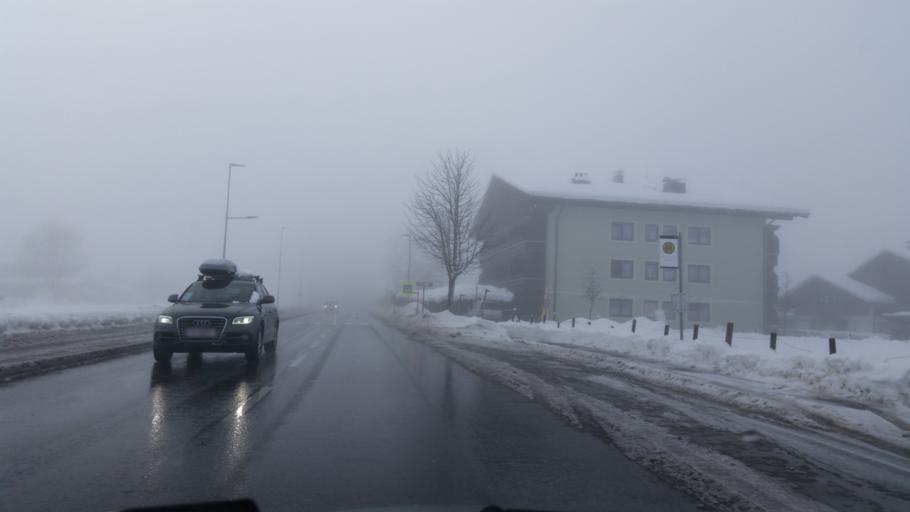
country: AT
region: Tyrol
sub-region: Politischer Bezirk Kitzbuhel
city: Sankt Johann in Tirol
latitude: 47.5273
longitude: 12.4325
